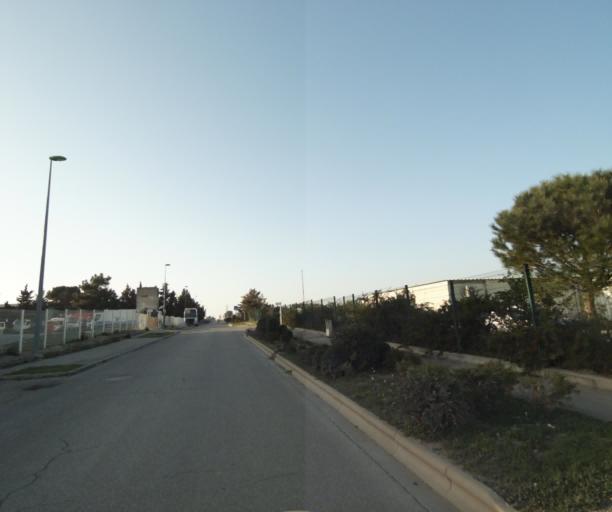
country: FR
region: Provence-Alpes-Cote d'Azur
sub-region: Departement des Bouches-du-Rhone
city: Saint-Victoret
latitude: 43.4279
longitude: 5.2417
